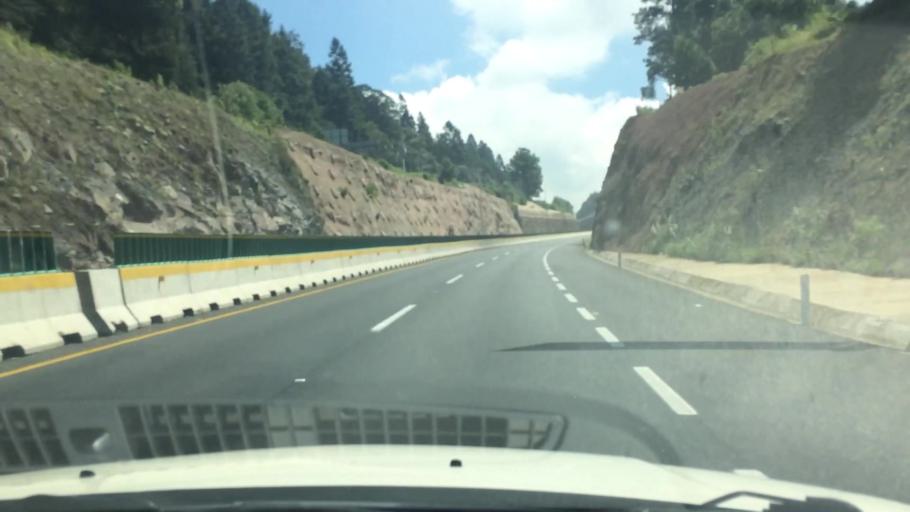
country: MX
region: Morelos
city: San Jeronimo Acazulco
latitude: 19.2986
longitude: -99.4004
